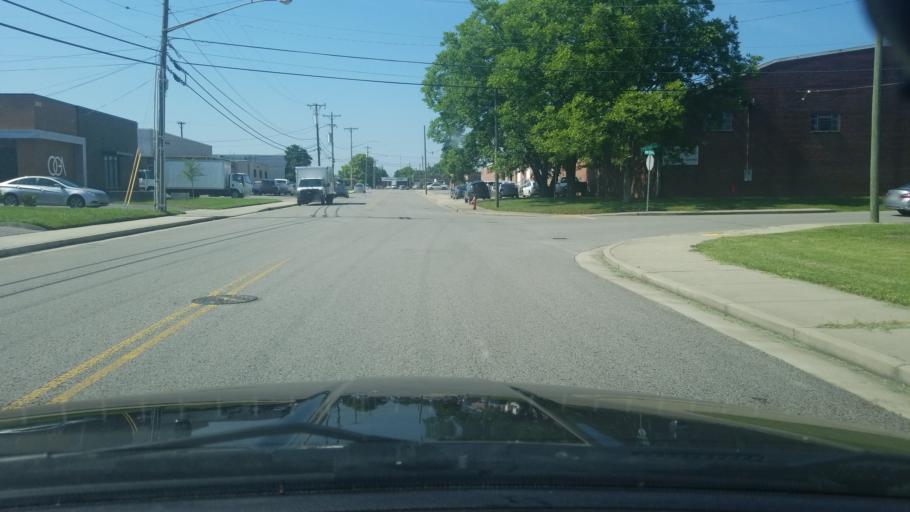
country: US
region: Tennessee
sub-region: Davidson County
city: Oak Hill
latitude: 36.1083
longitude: -86.7539
